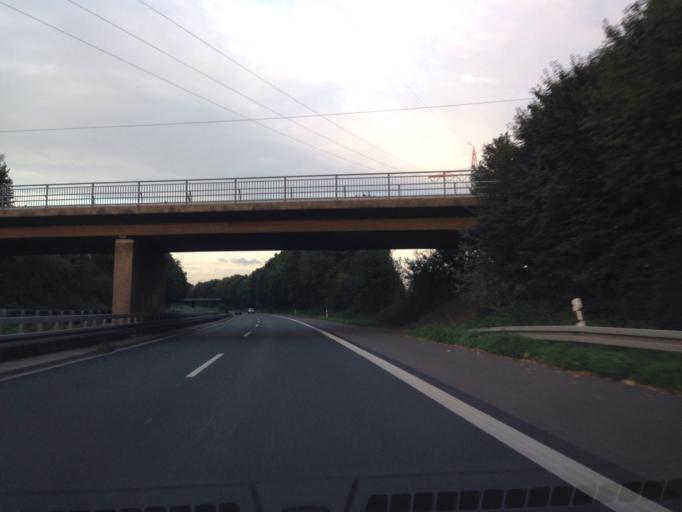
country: DE
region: North Rhine-Westphalia
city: Erkelenz
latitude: 51.0688
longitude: 6.3255
